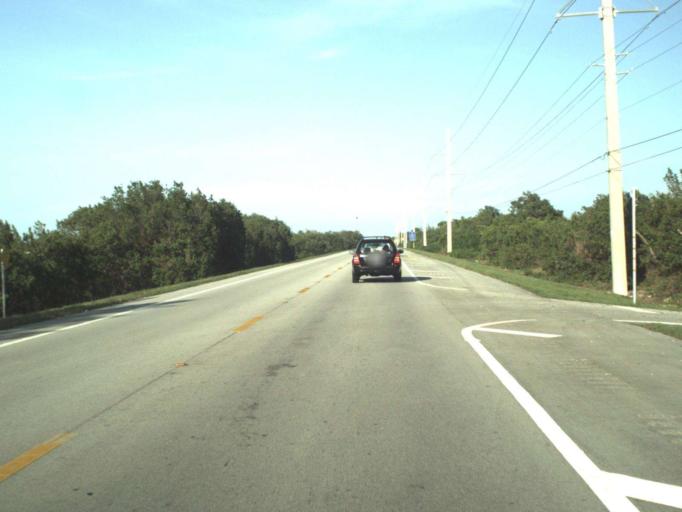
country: US
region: Florida
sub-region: Monroe County
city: Marathon
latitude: 24.7868
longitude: -80.8960
